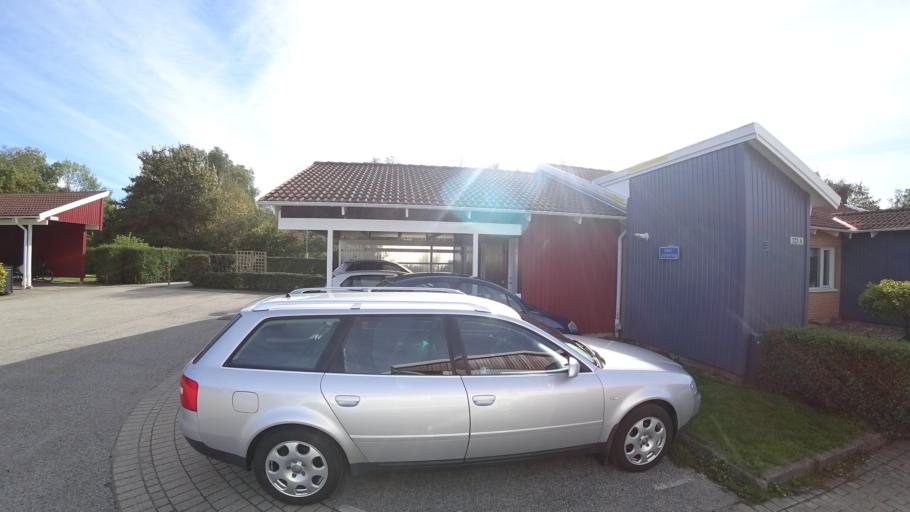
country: SE
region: Skane
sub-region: Kavlinge Kommun
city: Kaevlinge
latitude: 55.8026
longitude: 13.1034
